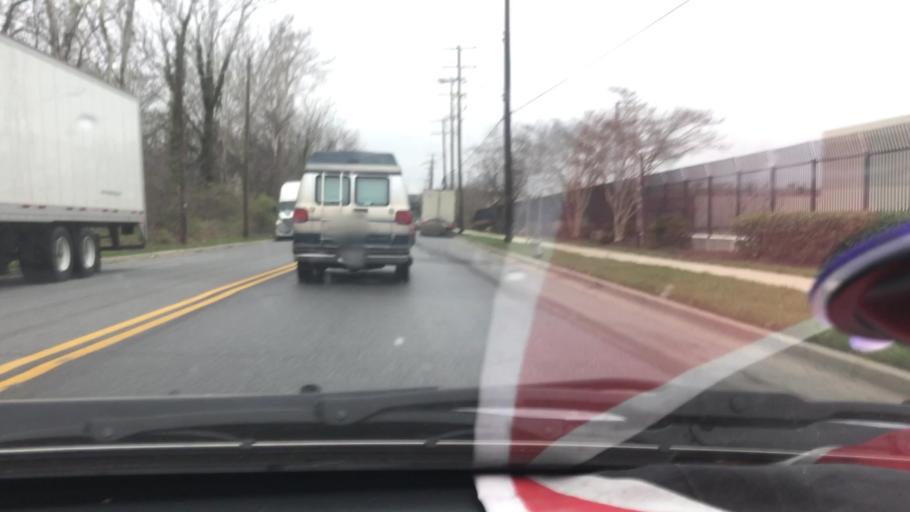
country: US
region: Maryland
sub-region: Prince George's County
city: Seat Pleasant
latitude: 38.9084
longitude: -76.9025
